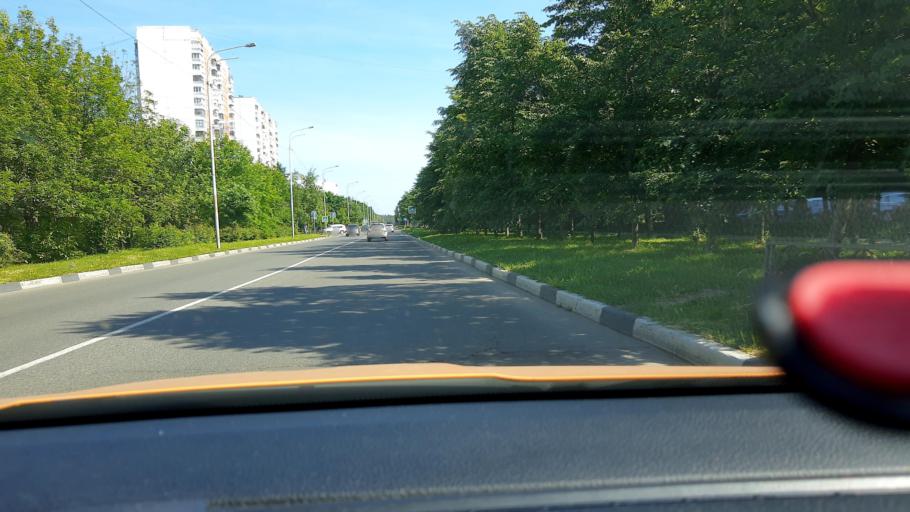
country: RU
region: Moskovskaya
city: Krasnoznamensk
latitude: 55.5934
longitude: 37.0354
